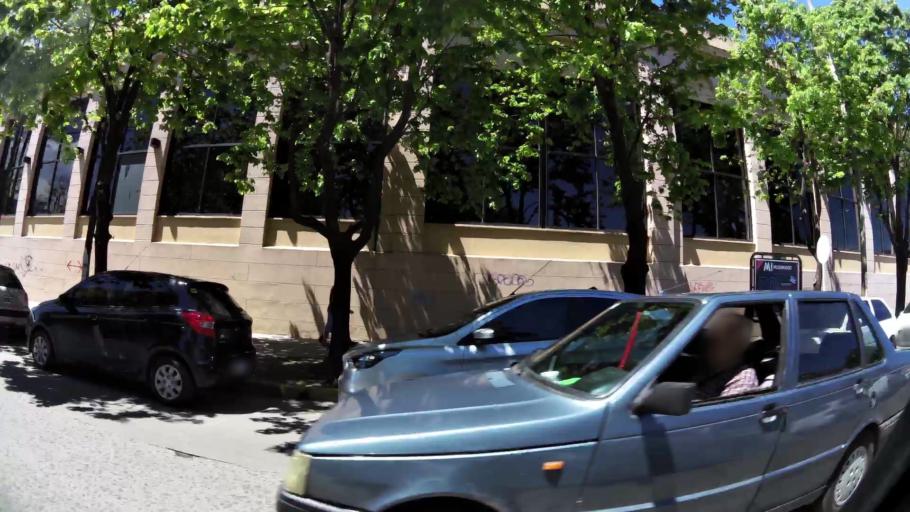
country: AR
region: Buenos Aires
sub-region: Partido de Quilmes
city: Quilmes
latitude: -34.7275
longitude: -58.2595
